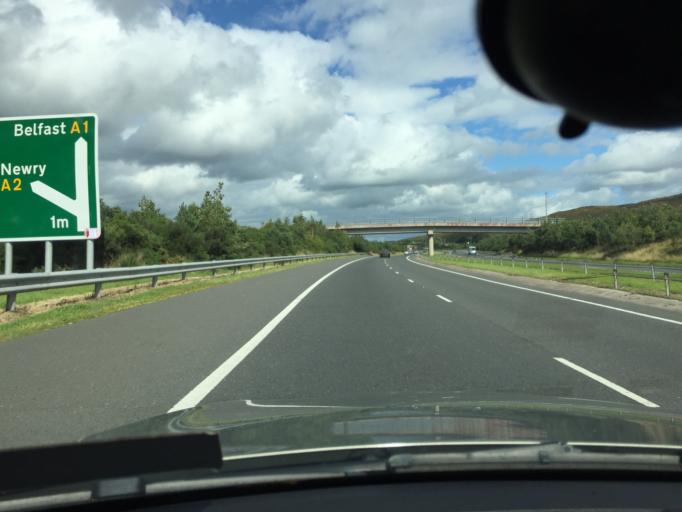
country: GB
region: Northern Ireland
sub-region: Newry and Mourne District
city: Newry
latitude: 54.1322
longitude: -6.3525
